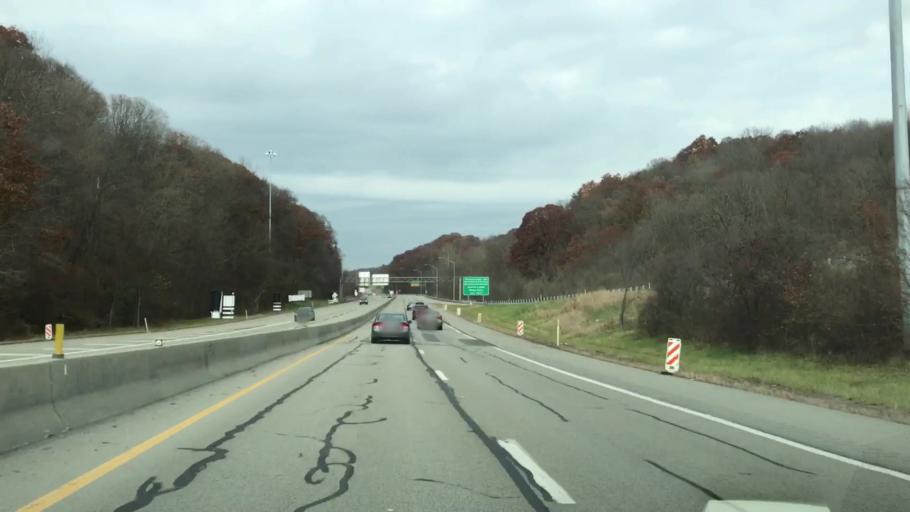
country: US
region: Pennsylvania
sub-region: Allegheny County
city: Enlow
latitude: 40.4703
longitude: -80.1989
